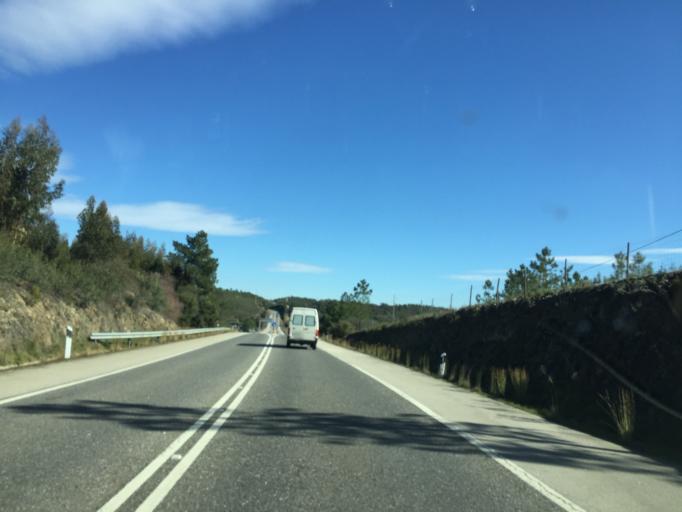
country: ES
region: Extremadura
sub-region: Provincia de Caceres
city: Cedillo
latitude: 39.7354
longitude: -7.6589
